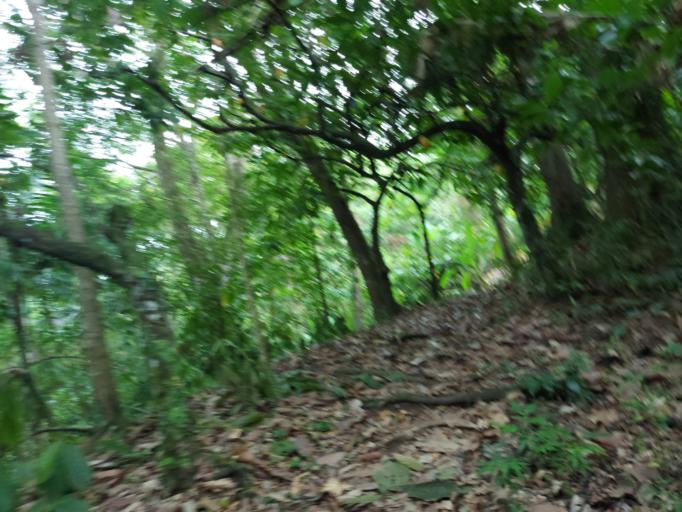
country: PA
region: Bocas del Toro
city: Barranco
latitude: 9.6402
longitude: -82.7835
